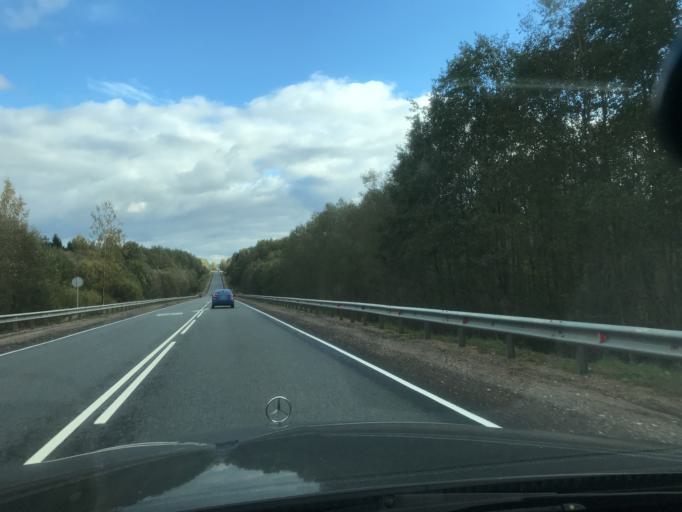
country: RU
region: Pskov
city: Opochka
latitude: 56.6392
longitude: 28.7885
